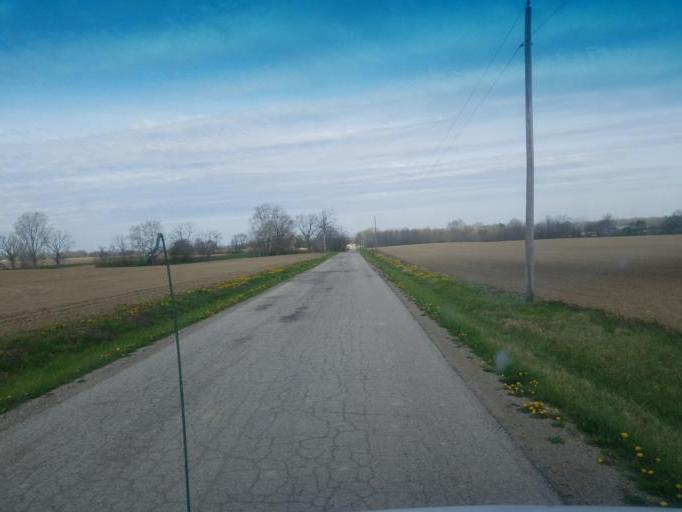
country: US
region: Ohio
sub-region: Delaware County
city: Ashley
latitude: 40.4392
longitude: -82.9626
